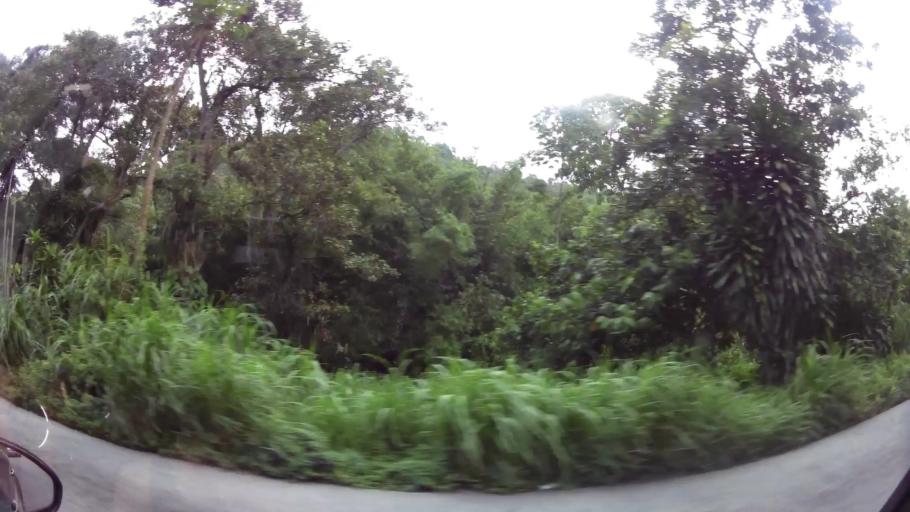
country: TT
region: San Juan/Laventille
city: Laventille
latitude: 10.6868
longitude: -61.4580
